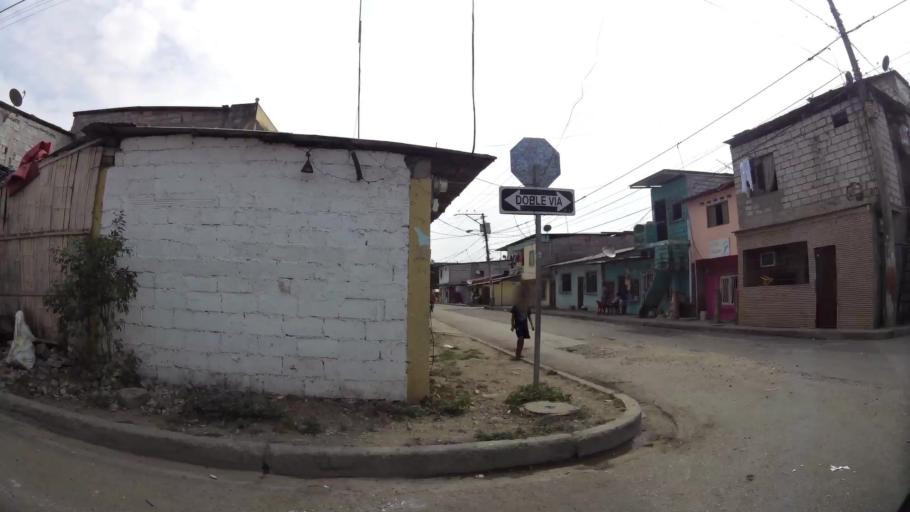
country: EC
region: Guayas
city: Guayaquil
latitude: -2.2399
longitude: -79.9106
